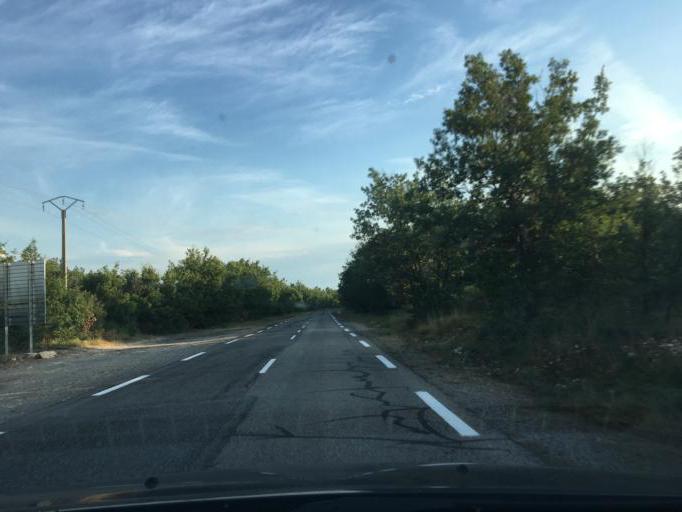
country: FR
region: Provence-Alpes-Cote d'Azur
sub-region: Departement du Var
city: Aups
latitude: 43.6957
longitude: 6.2182
